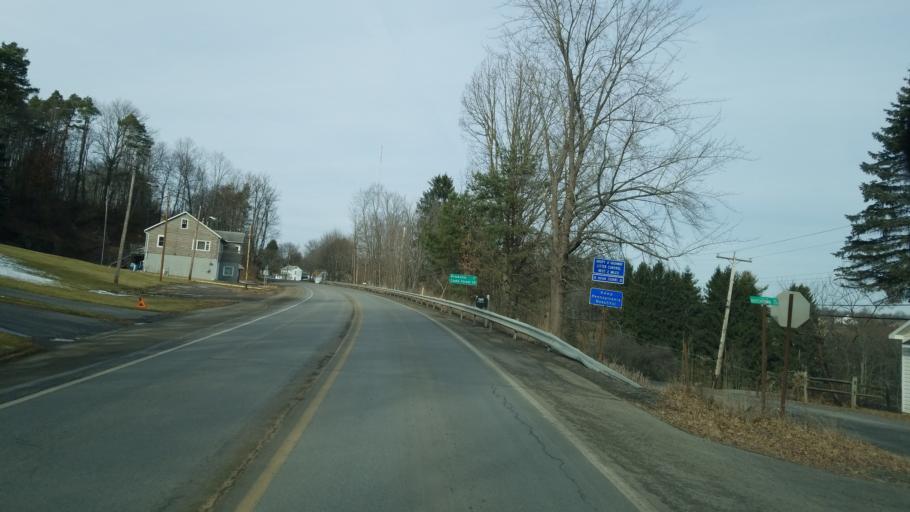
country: US
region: Pennsylvania
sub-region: Jefferson County
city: Punxsutawney
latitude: 40.9526
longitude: -78.9977
